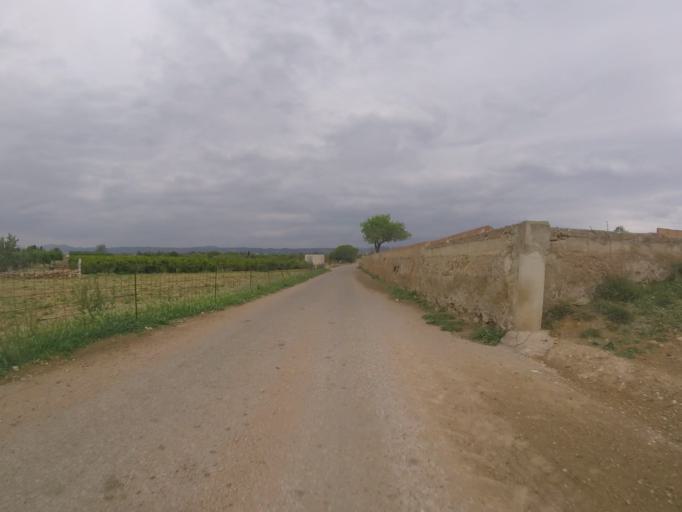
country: ES
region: Valencia
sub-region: Provincia de Castello
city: Torreblanca
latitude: 40.2144
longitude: 0.2382
